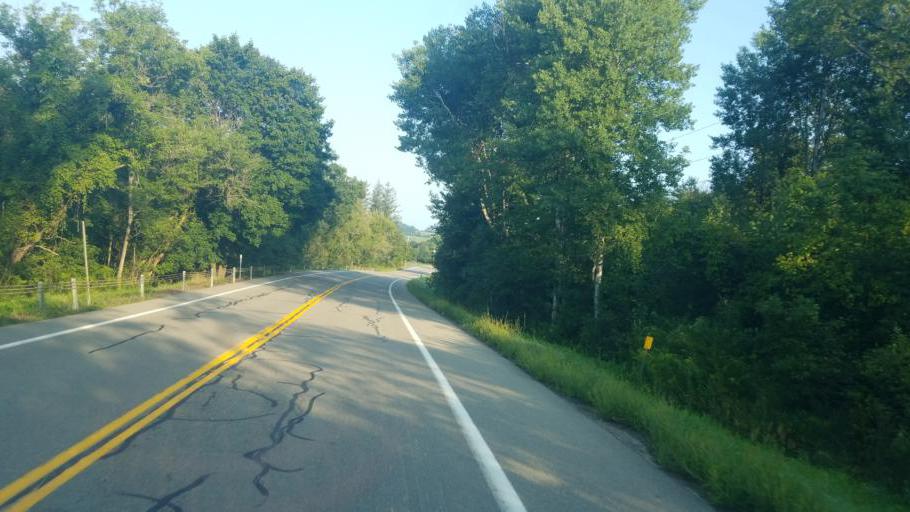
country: US
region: Pennsylvania
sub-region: Tioga County
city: Westfield
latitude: 42.0213
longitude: -77.5256
